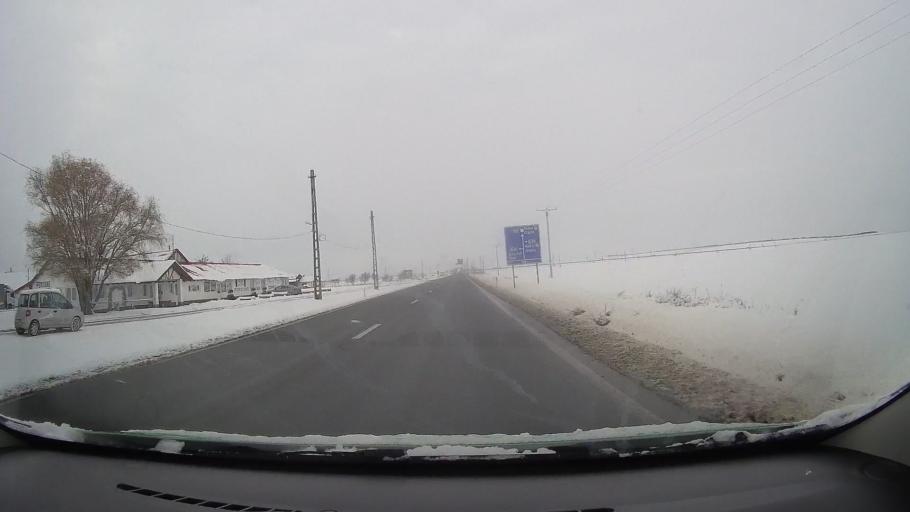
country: RO
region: Alba
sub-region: Municipiul Sebes
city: Lancram
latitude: 45.9701
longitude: 23.5272
